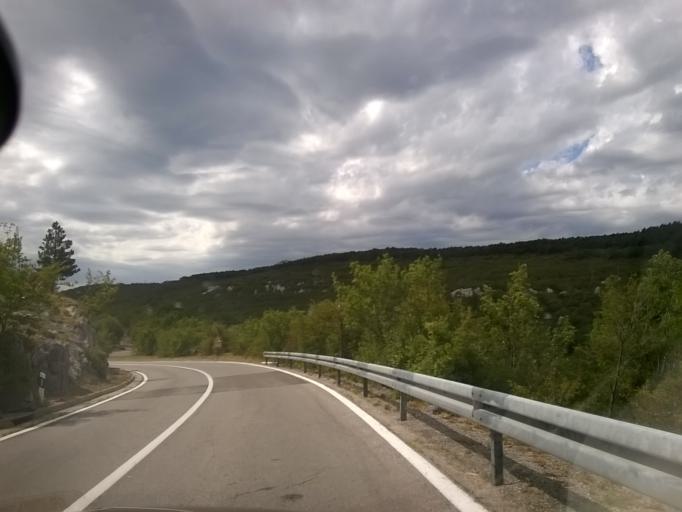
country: HR
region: Licko-Senjska
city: Karlobag
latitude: 44.5241
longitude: 15.1292
